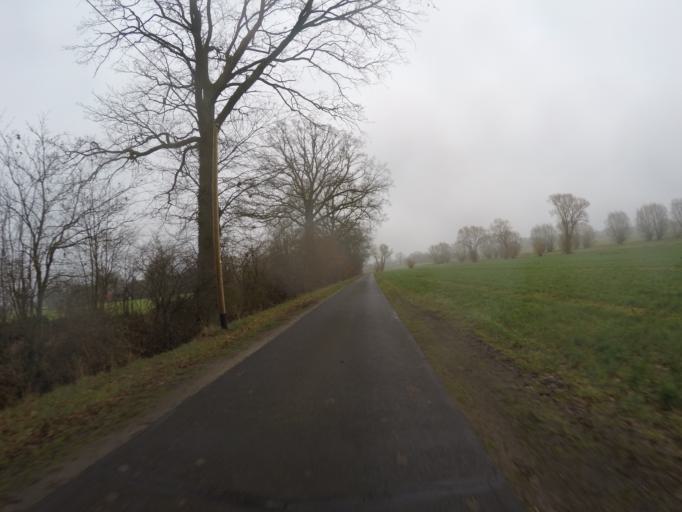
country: DE
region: Schleswig-Holstein
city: Bilsen
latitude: 53.7545
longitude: 9.8951
